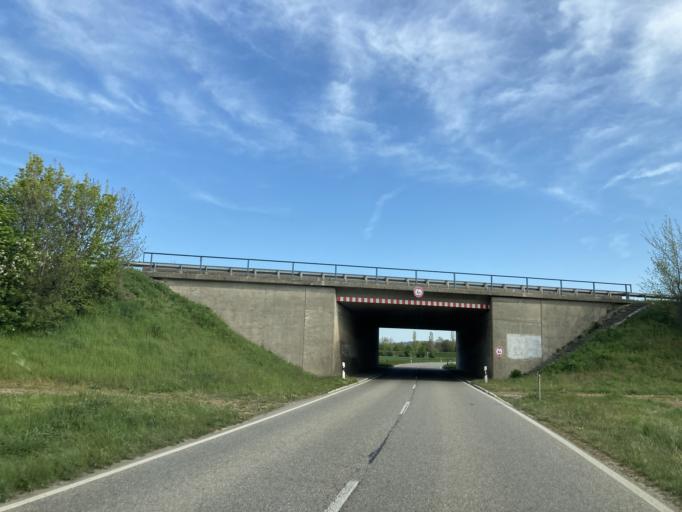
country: DE
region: Baden-Wuerttemberg
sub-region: Freiburg Region
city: Hartheim
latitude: 47.9502
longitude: 7.6648
